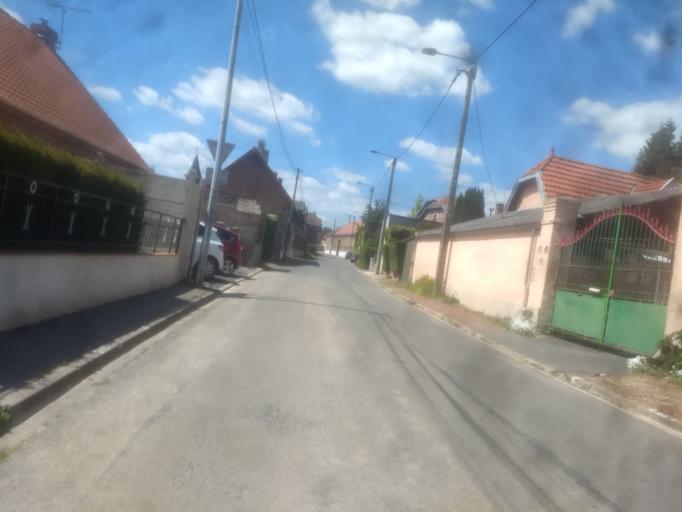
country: FR
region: Nord-Pas-de-Calais
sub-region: Departement du Pas-de-Calais
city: Riviere
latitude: 50.2452
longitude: 2.7187
